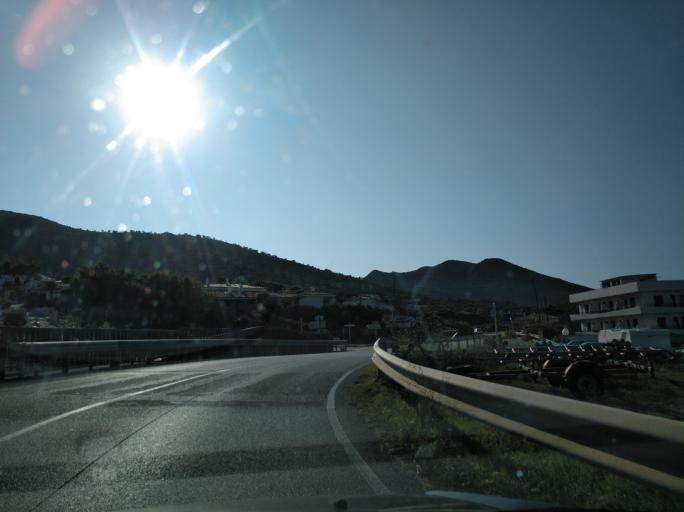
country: ES
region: Catalonia
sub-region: Provincia de Girona
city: Llanca
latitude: 42.3341
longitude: 3.1979
